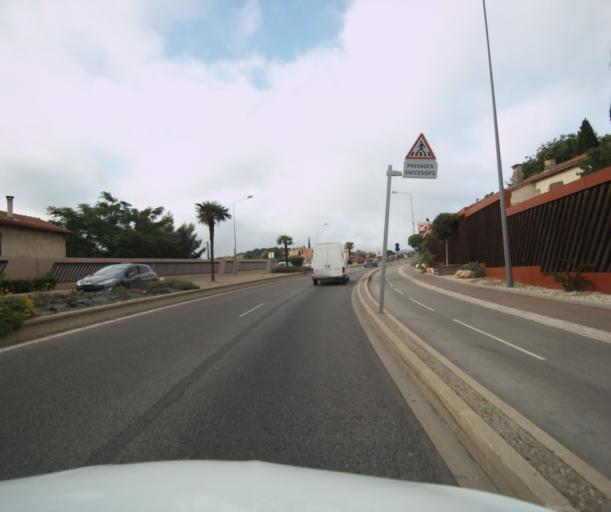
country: FR
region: Provence-Alpes-Cote d'Azur
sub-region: Departement du Var
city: Six-Fours-les-Plages
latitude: 43.1023
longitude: 5.8541
